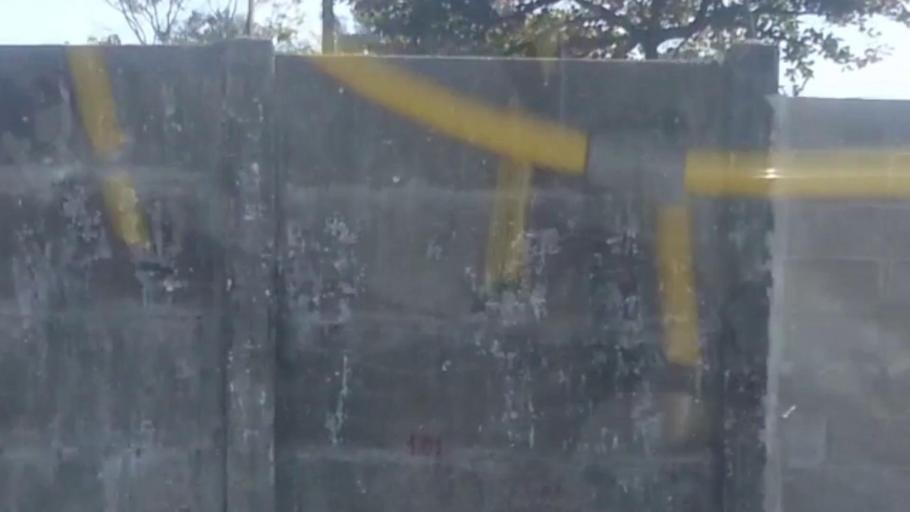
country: BR
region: Rio de Janeiro
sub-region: Nilopolis
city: Nilopolis
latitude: -22.8617
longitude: -43.3998
